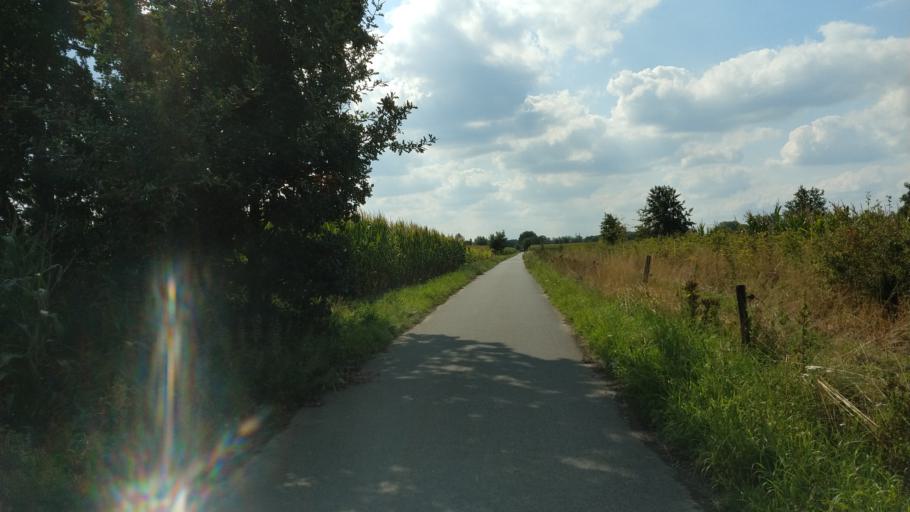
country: BE
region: Flanders
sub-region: Provincie Oost-Vlaanderen
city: Assenede
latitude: 51.2421
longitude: 3.6916
